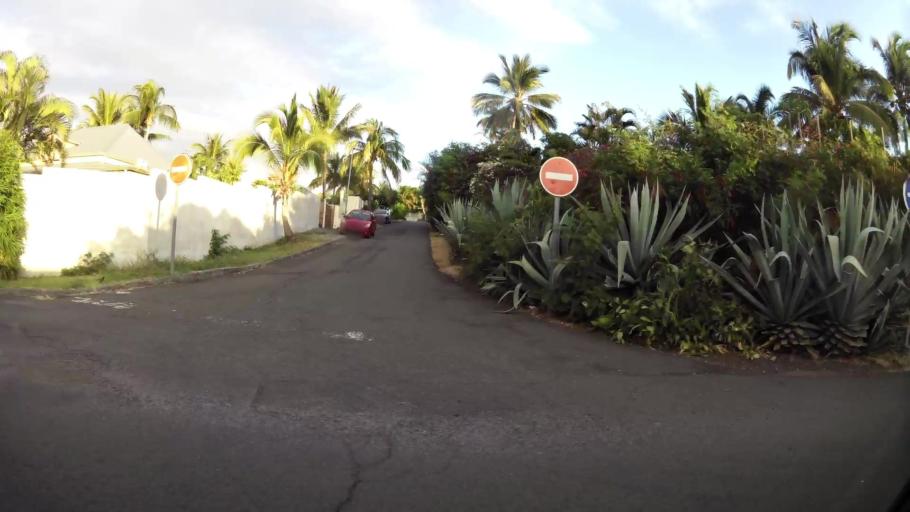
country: RE
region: Reunion
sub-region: Reunion
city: Saint-Paul
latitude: -21.0411
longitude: 55.2224
